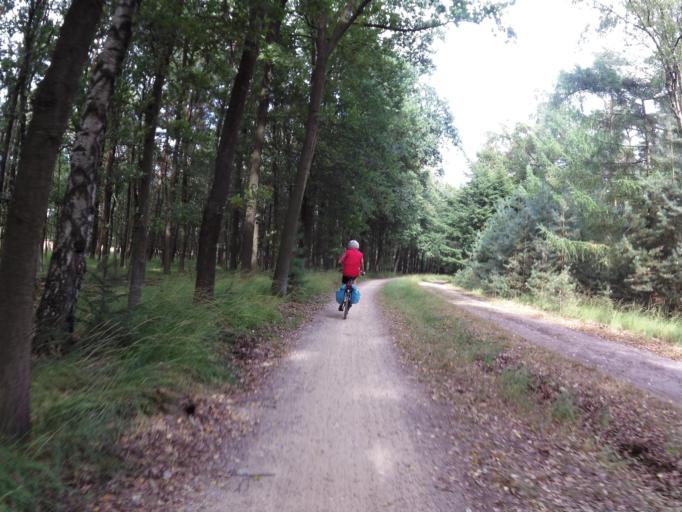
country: NL
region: North Brabant
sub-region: Gemeente Valkenswaard
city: Valkenswaard
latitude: 51.3361
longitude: 5.4965
